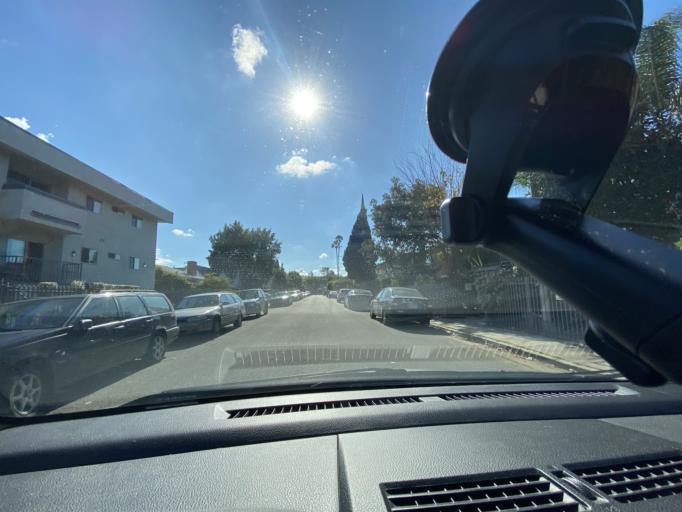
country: US
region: California
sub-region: Los Angeles County
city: Culver City
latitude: 34.0400
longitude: -118.3782
